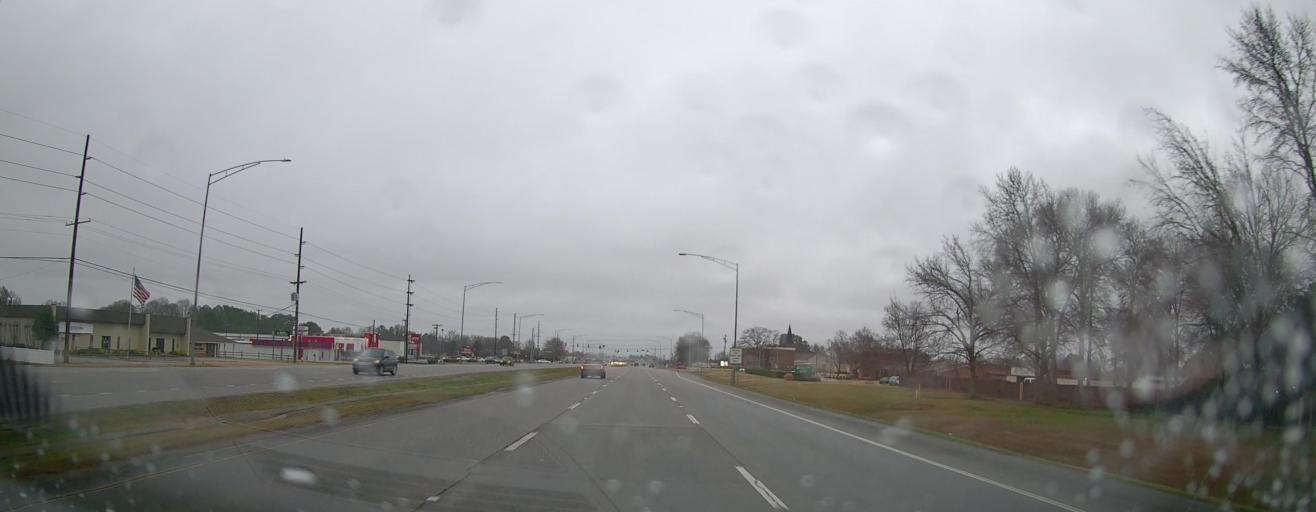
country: US
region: Alabama
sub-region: Morgan County
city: Decatur
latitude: 34.5856
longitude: -87.0255
